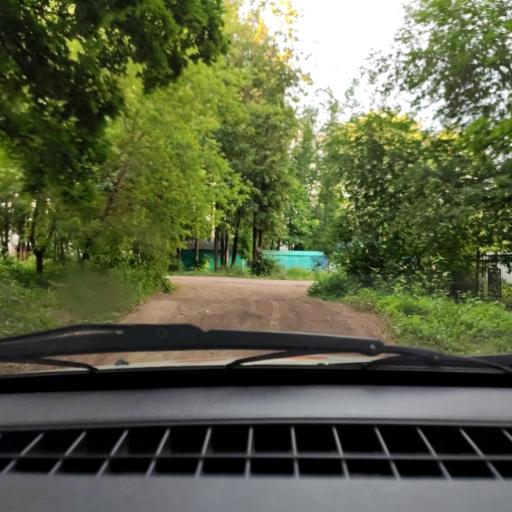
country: RU
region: Bashkortostan
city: Ufa
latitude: 54.7560
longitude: 55.9906
